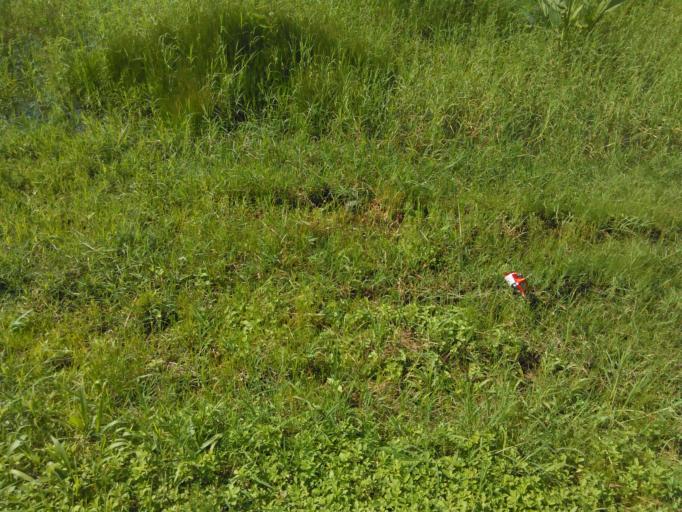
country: MX
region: Nayarit
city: Tepic
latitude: 21.4859
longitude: -104.8584
